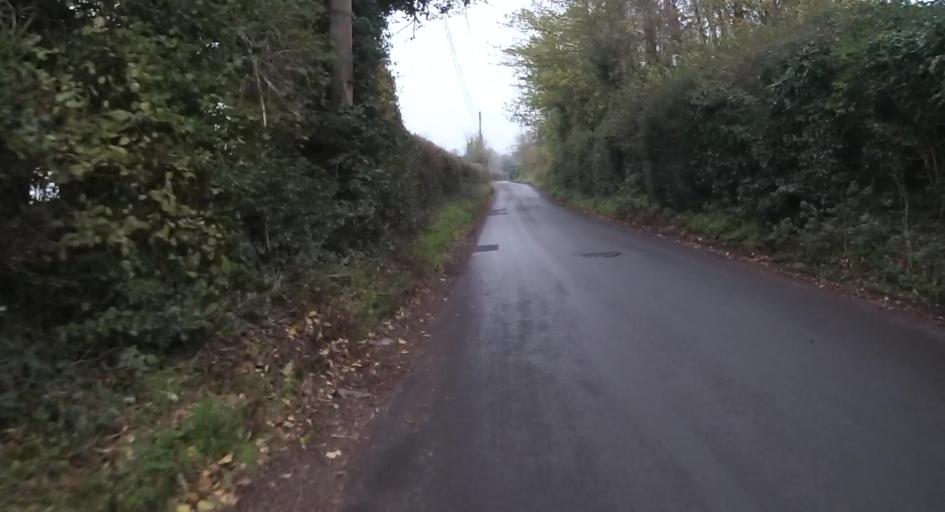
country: GB
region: England
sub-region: Hampshire
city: Long Sutton
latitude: 51.1918
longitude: -0.9105
